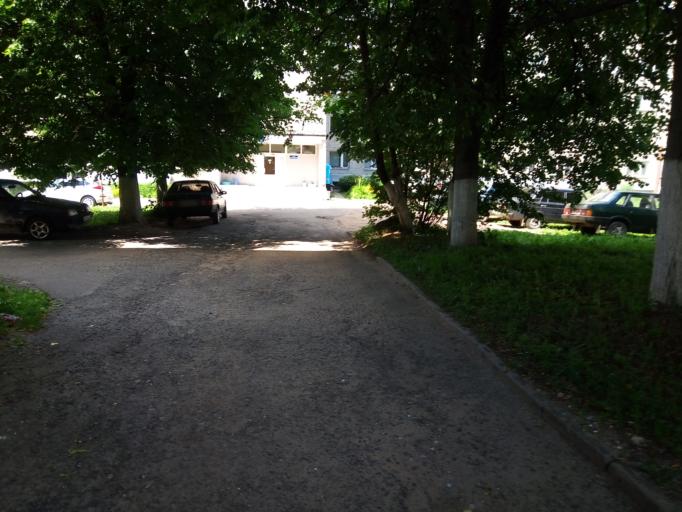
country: RU
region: Kursk
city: Kursk
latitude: 51.7456
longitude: 36.1811
